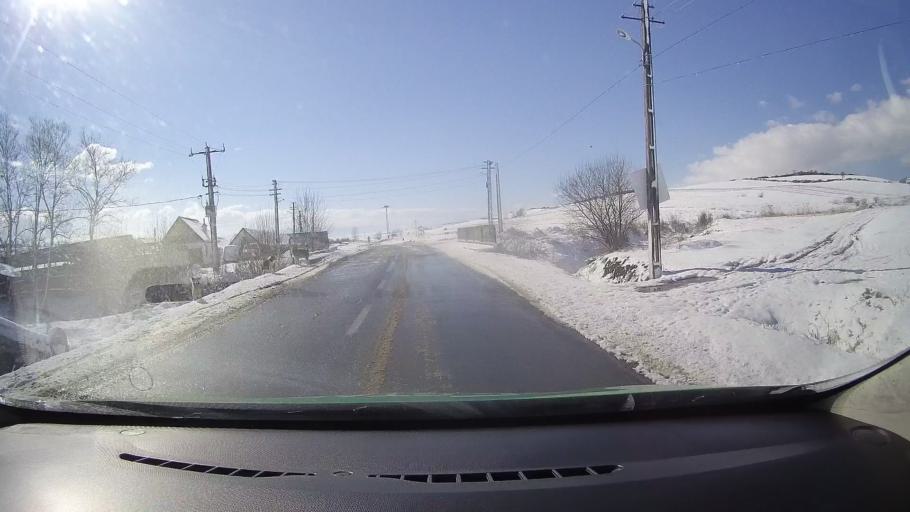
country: RO
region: Sibiu
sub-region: Comuna Vurpar
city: Vurpar
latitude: 45.8864
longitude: 24.3310
